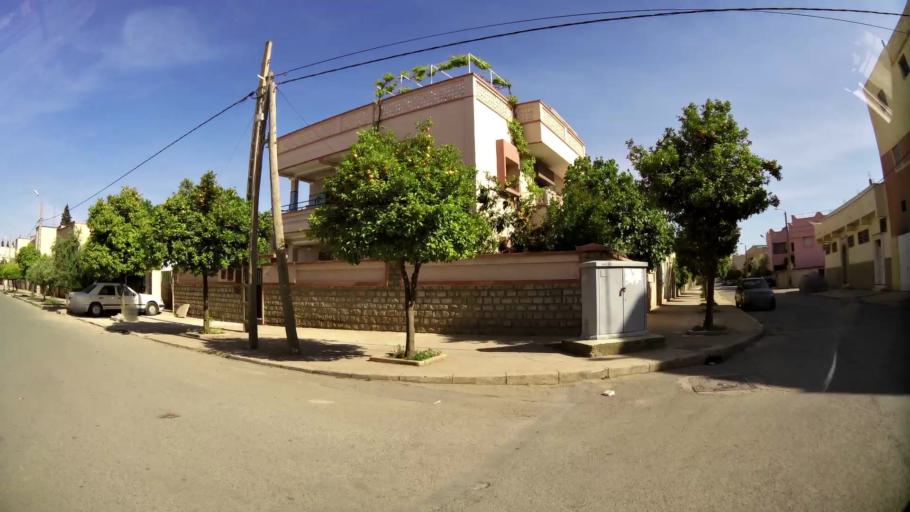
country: MA
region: Oriental
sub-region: Oujda-Angad
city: Oujda
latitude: 34.6686
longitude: -1.9105
